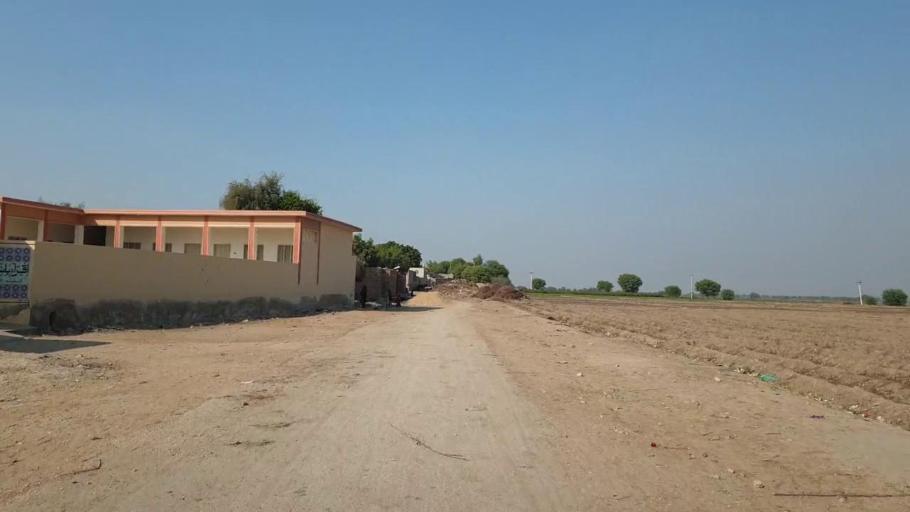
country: PK
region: Sindh
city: Sehwan
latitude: 26.4483
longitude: 67.8176
